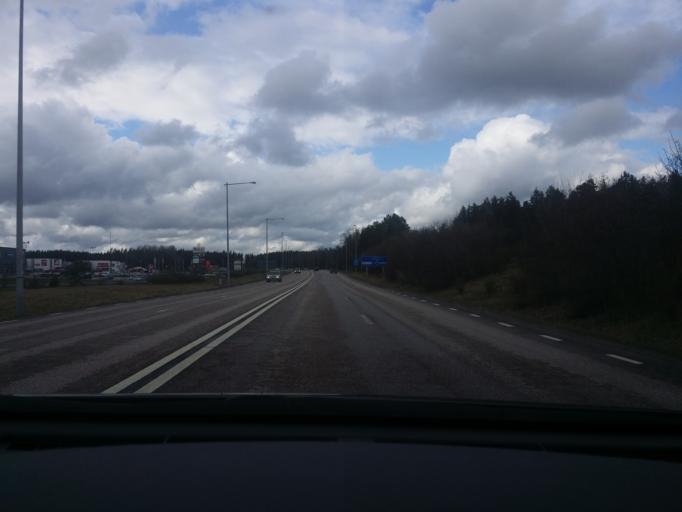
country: SE
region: Vaestmanland
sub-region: Vasteras
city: Vasteras
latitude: 59.6156
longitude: 16.4679
